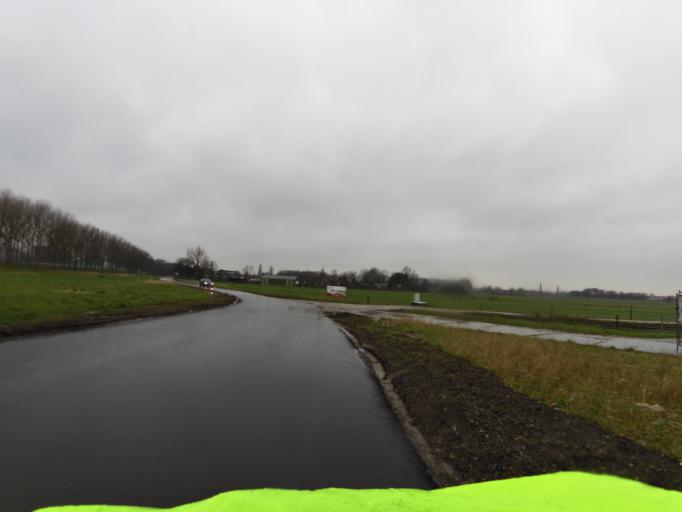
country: NL
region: South Holland
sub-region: Gemeente Maassluis
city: Maassluis
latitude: 51.9240
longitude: 4.2797
